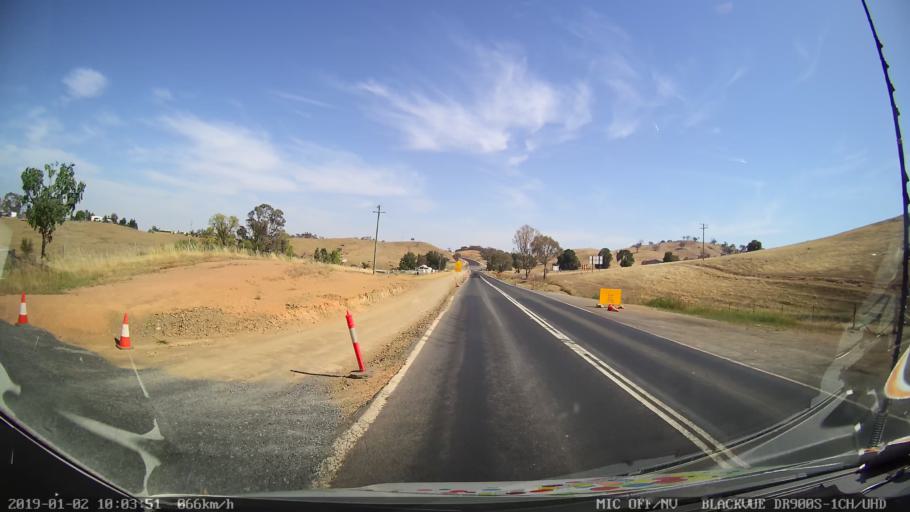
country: AU
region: New South Wales
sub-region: Gundagai
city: Gundagai
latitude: -35.1736
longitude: 148.1250
